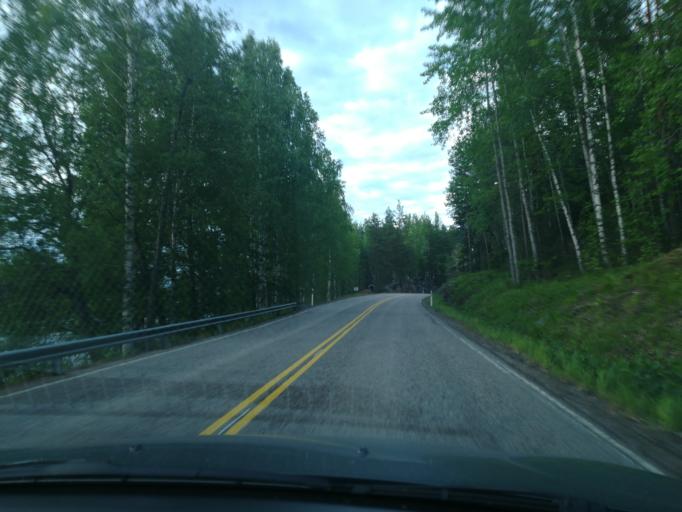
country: FI
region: Southern Savonia
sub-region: Mikkeli
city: Puumala
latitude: 61.5607
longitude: 27.9752
